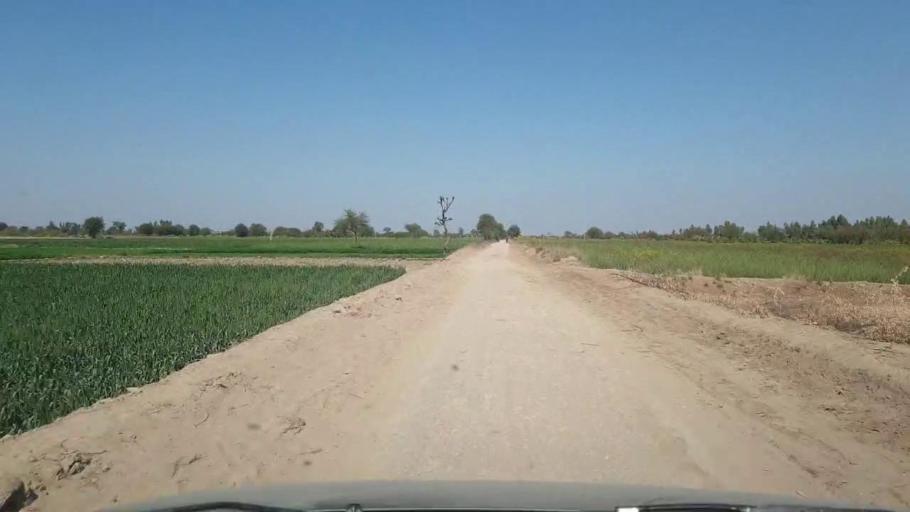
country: PK
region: Sindh
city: Samaro
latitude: 25.3063
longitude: 69.2684
